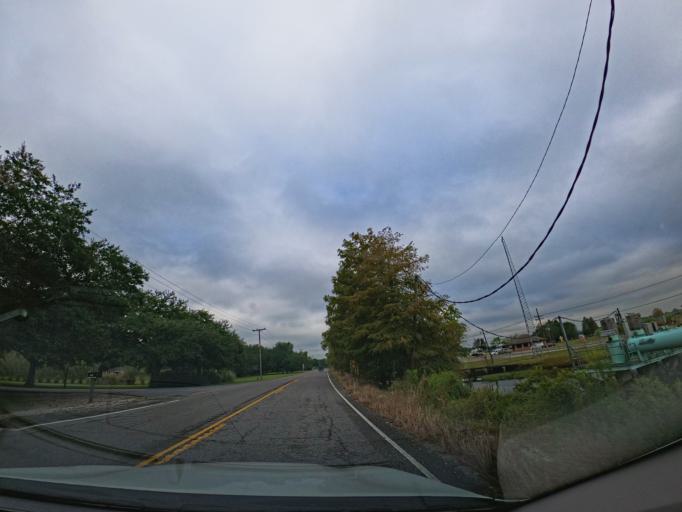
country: US
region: Louisiana
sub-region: Terrebonne Parish
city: Bayou Cane
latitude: 29.5598
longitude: -90.7905
